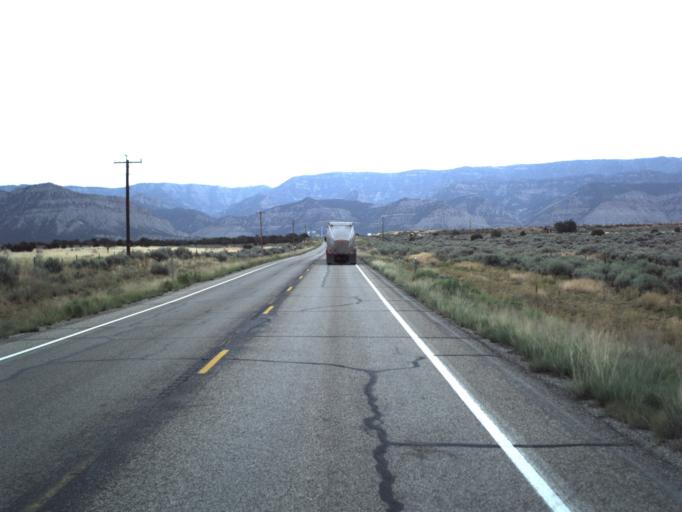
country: US
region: Utah
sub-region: Carbon County
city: East Carbon City
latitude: 39.5367
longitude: -110.4573
